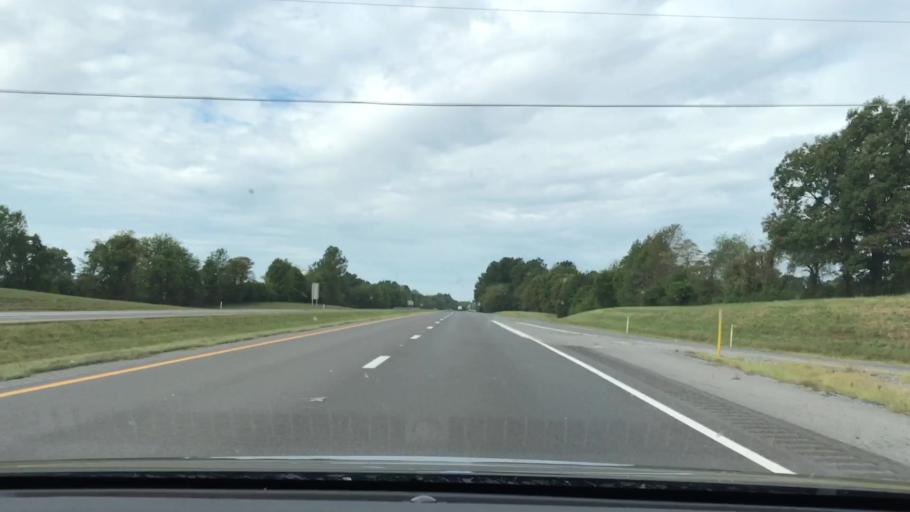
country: US
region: Kentucky
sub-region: Graves County
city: Mayfield
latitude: 36.7749
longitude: -88.5981
